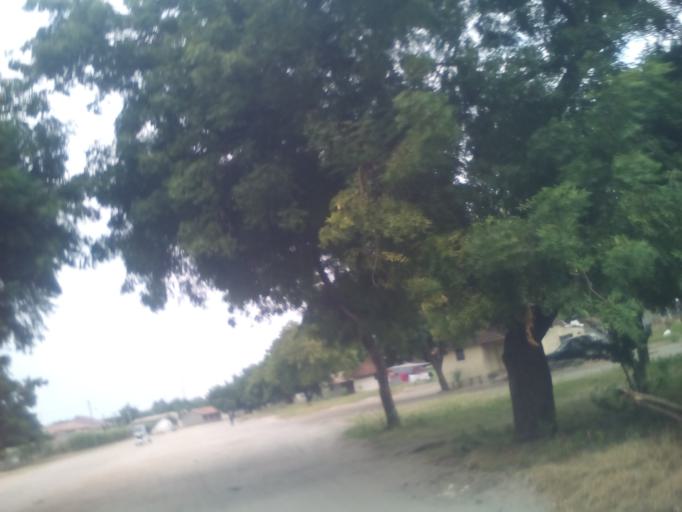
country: TZ
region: Dar es Salaam
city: Dar es Salaam
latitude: -6.8481
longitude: 39.2774
